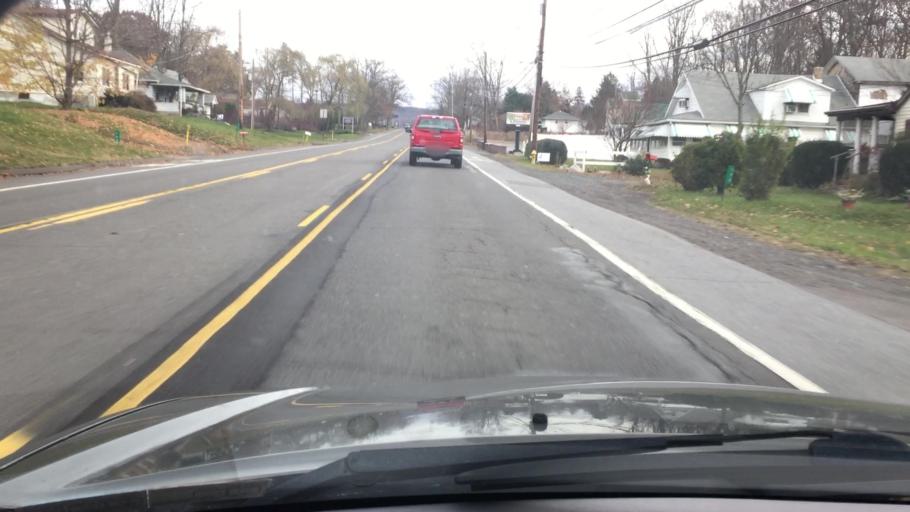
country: US
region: Pennsylvania
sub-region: Luzerne County
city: Mountain Top
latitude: 41.1521
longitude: -75.8941
